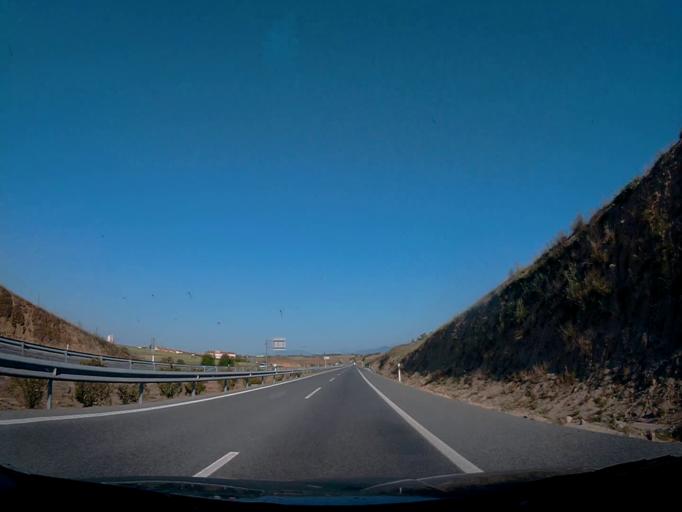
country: ES
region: Castille-La Mancha
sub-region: Province of Toledo
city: Santa Cruz del Retamar
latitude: 40.1256
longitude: -4.2274
